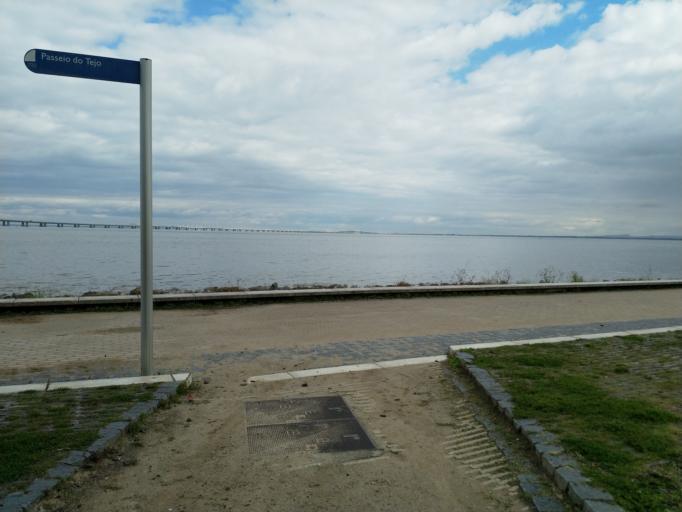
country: PT
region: Lisbon
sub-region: Loures
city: Moscavide
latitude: 38.7799
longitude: -9.0912
